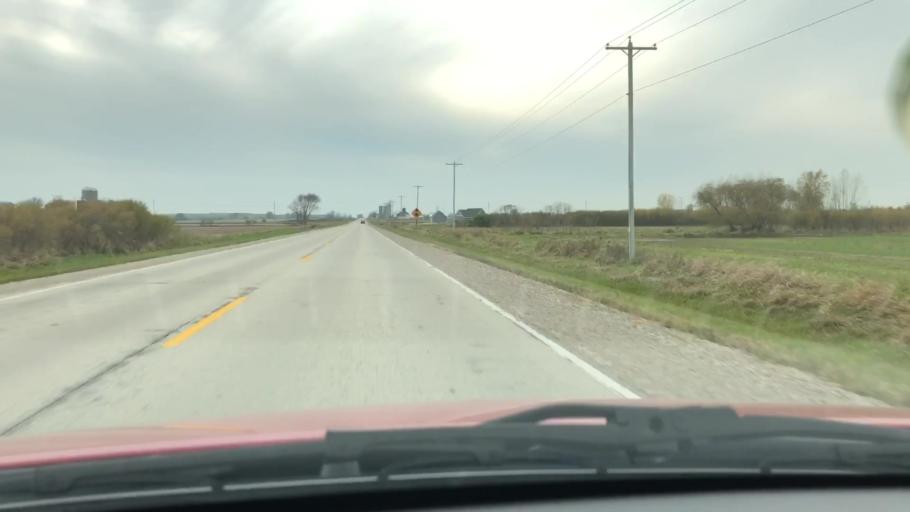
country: US
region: Wisconsin
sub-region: Outagamie County
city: Seymour
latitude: 44.4439
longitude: -88.2848
